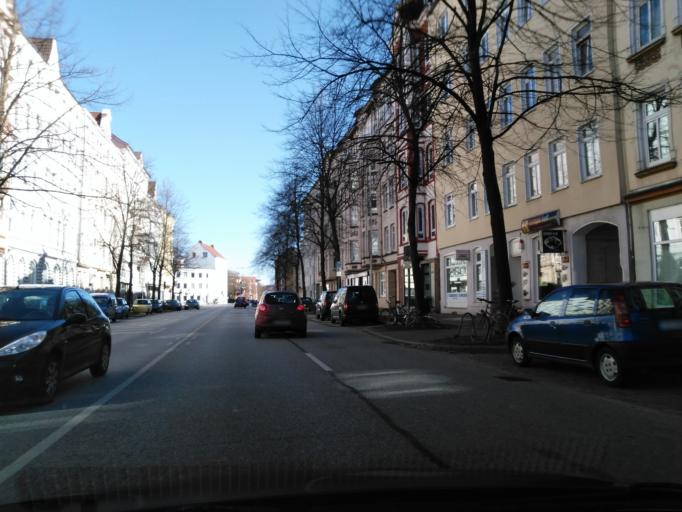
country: DE
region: Schleswig-Holstein
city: Kiel
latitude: 54.3317
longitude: 10.1258
